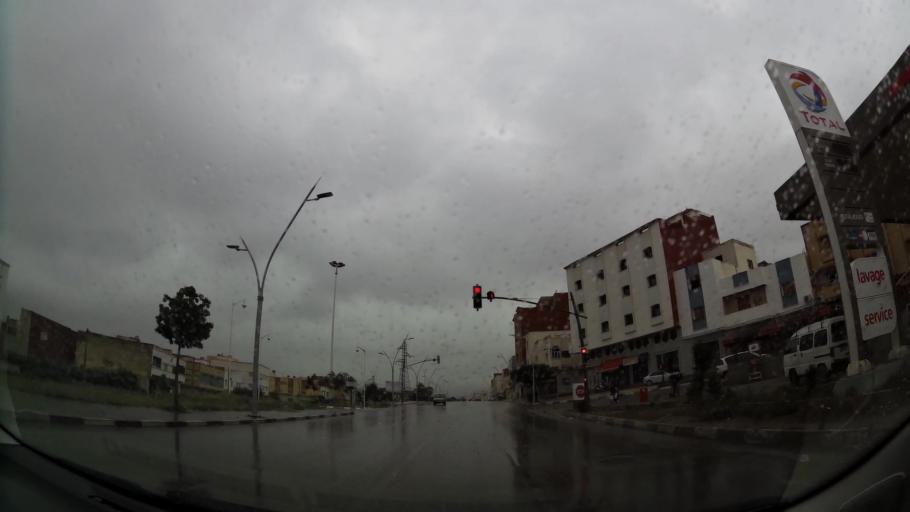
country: MA
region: Oriental
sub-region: Nador
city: Nador
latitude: 35.1565
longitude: -2.9750
